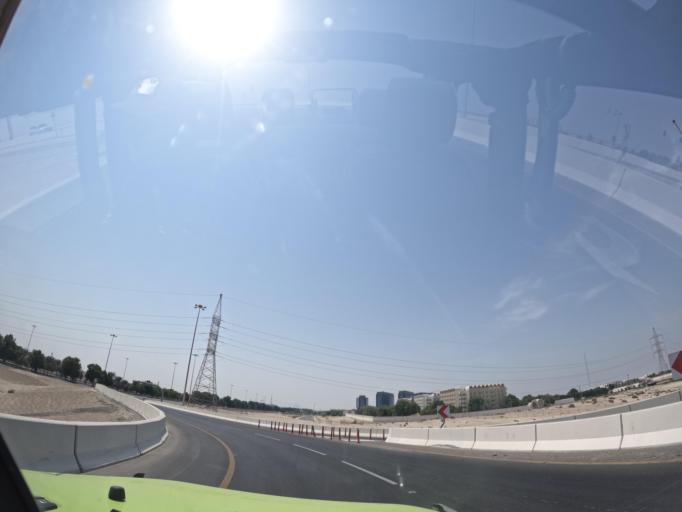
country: AE
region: Abu Dhabi
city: Abu Dhabi
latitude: 24.3278
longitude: 54.6223
